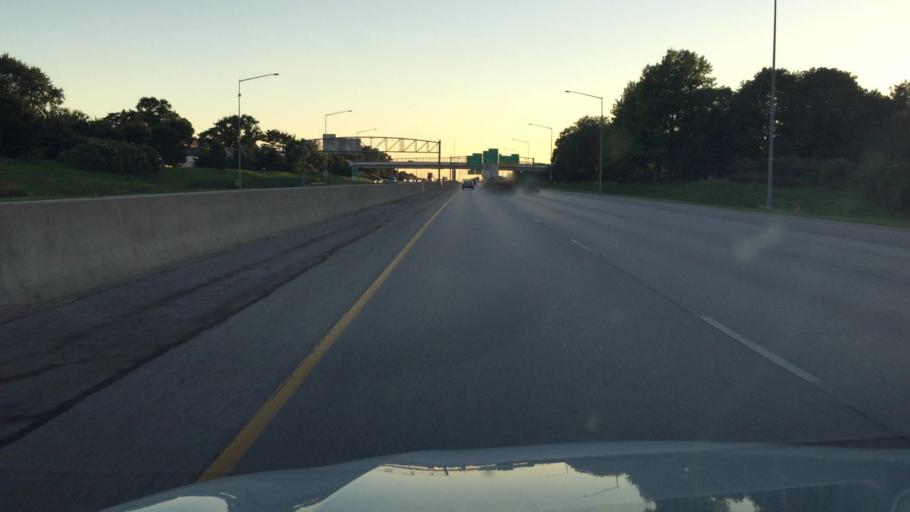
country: US
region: Iowa
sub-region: Polk County
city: Clive
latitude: 41.5923
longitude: -93.7572
